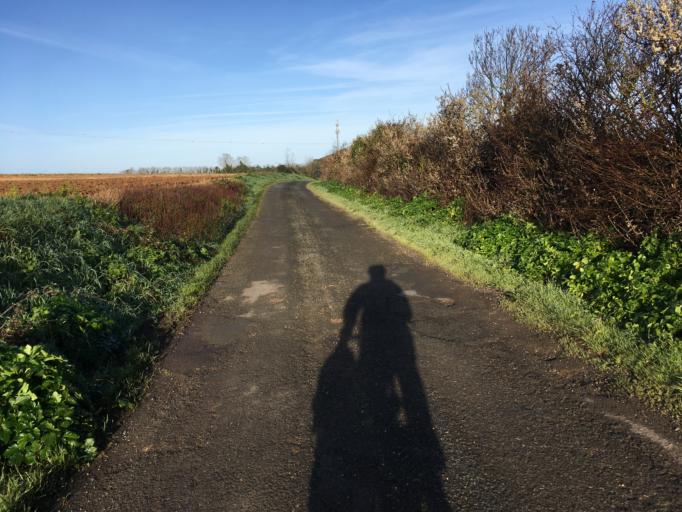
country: FR
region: Poitou-Charentes
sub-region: Departement de la Charente-Maritime
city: Nieul-sur-Mer
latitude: 46.1975
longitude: -1.1776
